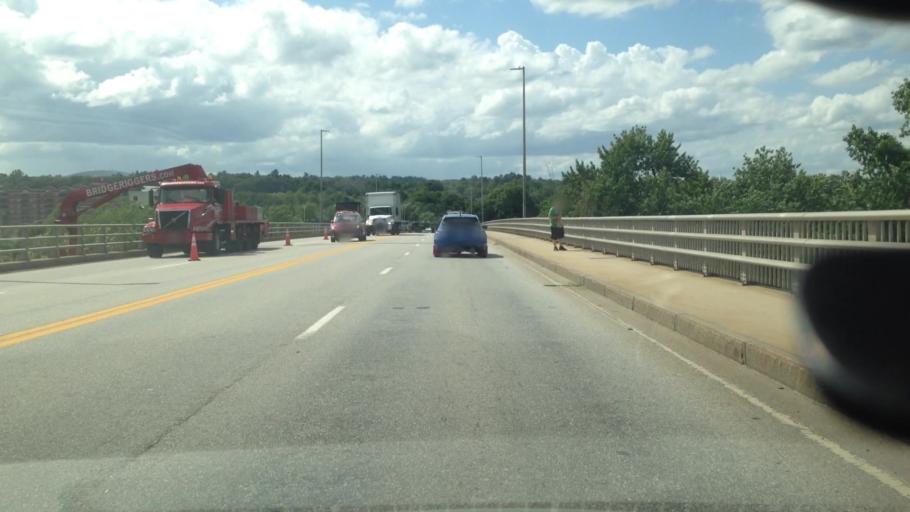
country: US
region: New Hampshire
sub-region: Hillsborough County
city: Manchester
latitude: 42.9741
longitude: -71.4708
